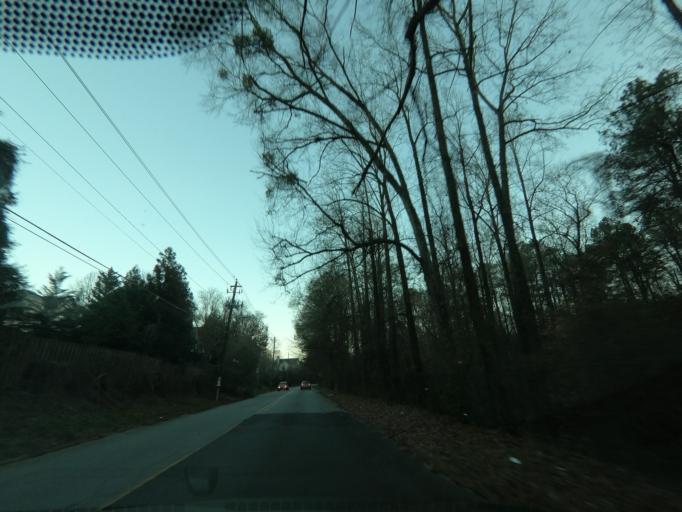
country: US
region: Georgia
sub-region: Cobb County
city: Vinings
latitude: 33.8155
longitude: -84.4583
